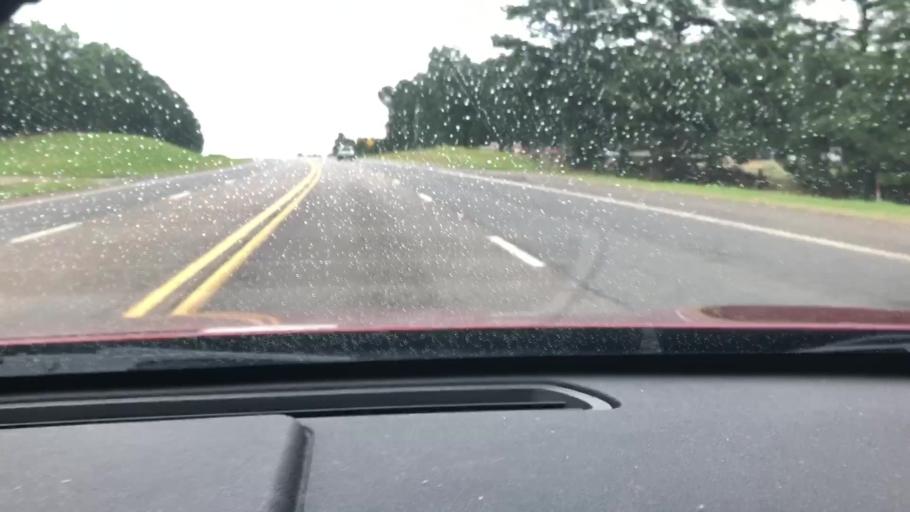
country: US
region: Arkansas
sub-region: Lafayette County
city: Lewisville
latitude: 33.3567
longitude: -93.5616
